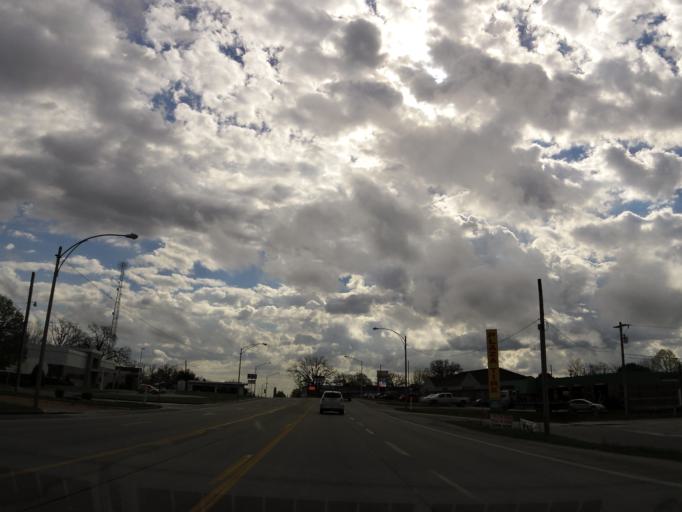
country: US
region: Missouri
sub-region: Butler County
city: Poplar Bluff
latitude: 36.7585
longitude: -90.4064
